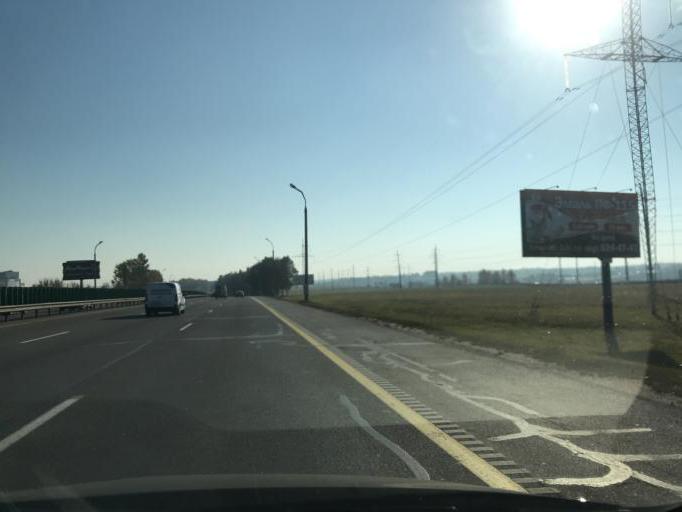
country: BY
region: Minsk
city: Malinovka
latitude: 53.8600
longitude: 27.4274
